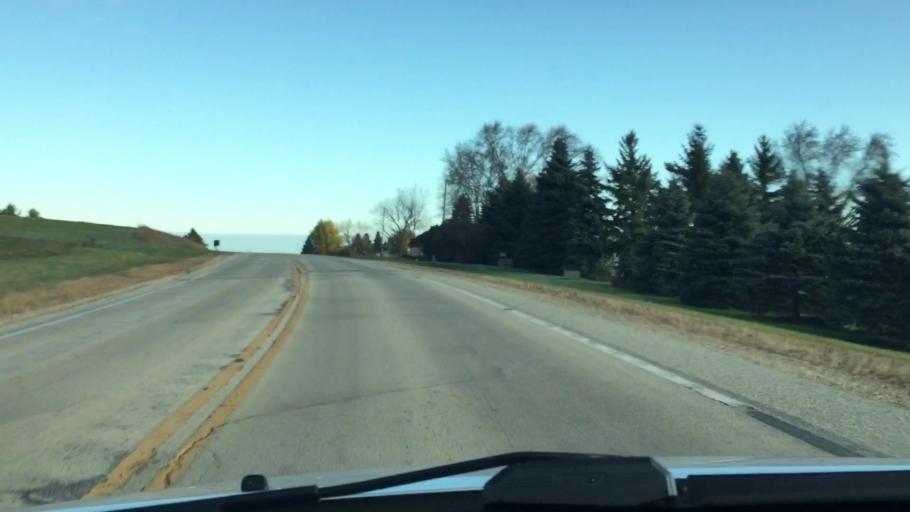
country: US
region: Wisconsin
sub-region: Washington County
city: Hartford
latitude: 43.2865
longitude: -88.4591
